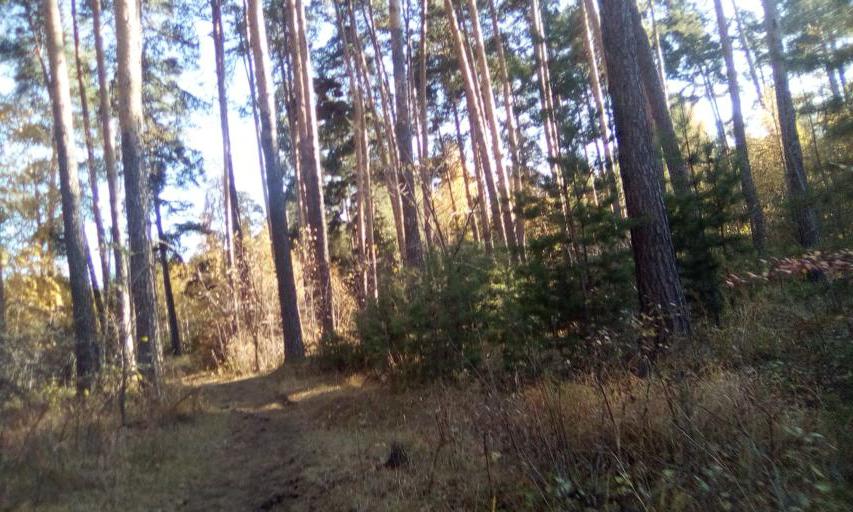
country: RU
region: Chelyabinsk
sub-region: Gorod Chelyabinsk
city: Chelyabinsk
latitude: 55.1614
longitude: 61.3552
